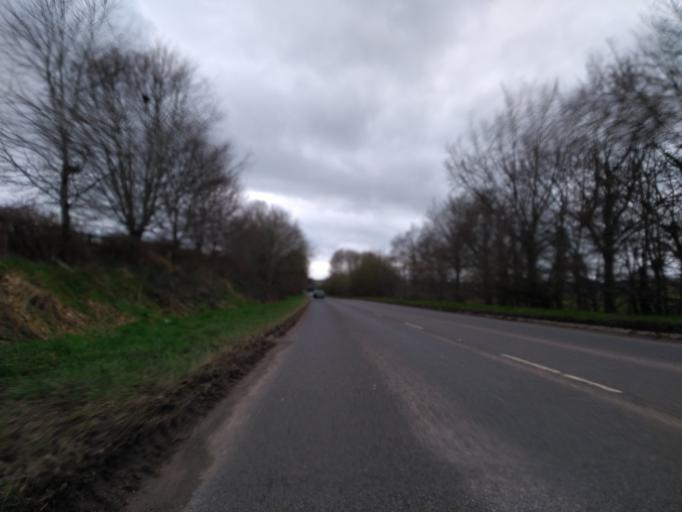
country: GB
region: England
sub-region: Devon
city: Crediton
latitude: 50.7734
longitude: -3.5987
